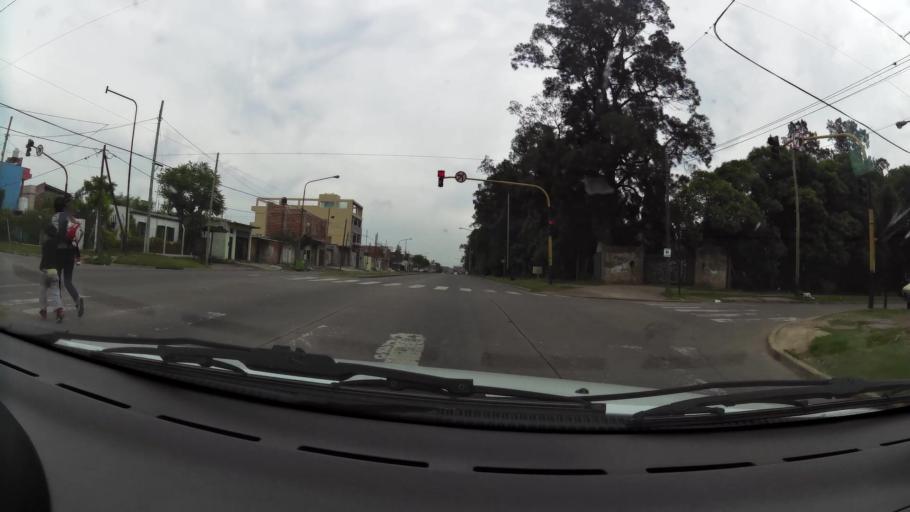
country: AR
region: Buenos Aires
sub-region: Partido de La Plata
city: La Plata
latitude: -34.9084
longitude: -57.9857
